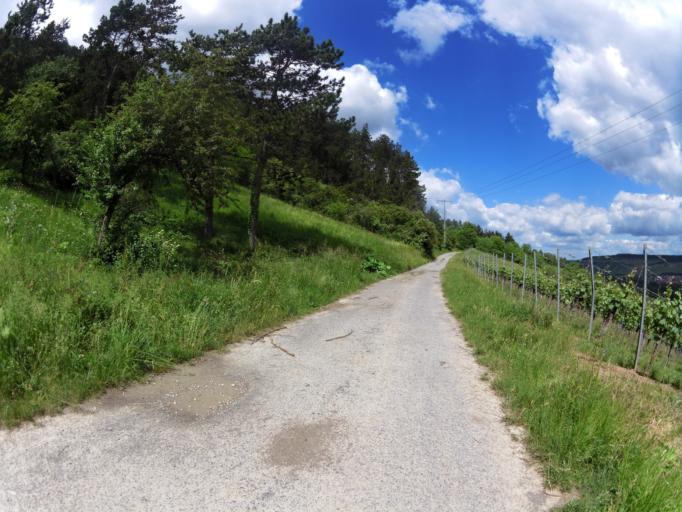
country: DE
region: Bavaria
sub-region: Regierungsbezirk Unterfranken
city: Erlabrunn
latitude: 49.8633
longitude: 9.8351
